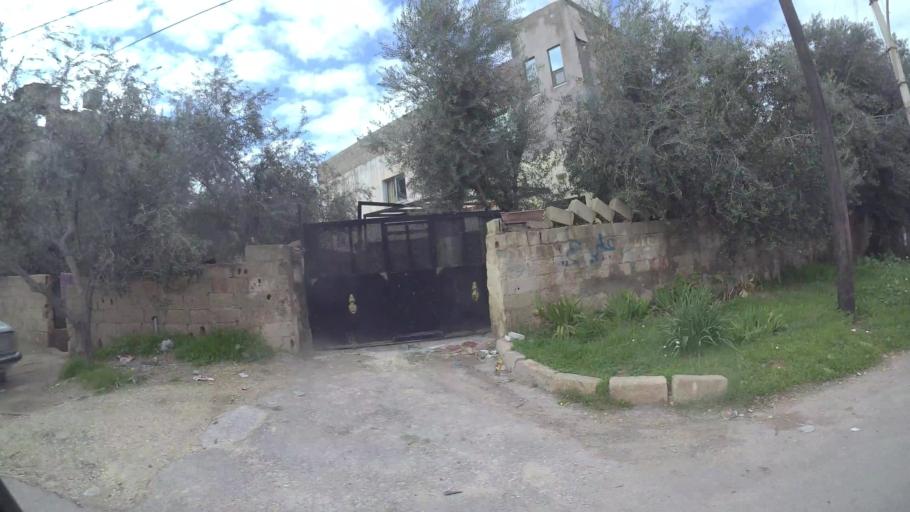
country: JO
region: Amman
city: Al Jubayhah
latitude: 32.0597
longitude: 35.8323
